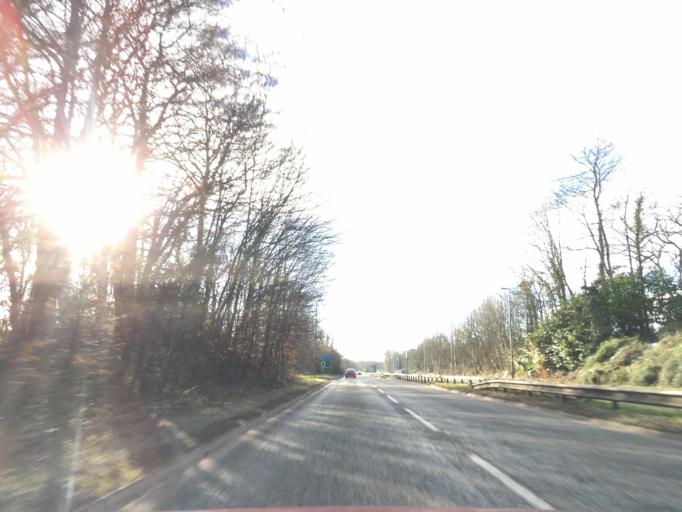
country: GB
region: Wales
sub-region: Torfaen County Borough
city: New Inn
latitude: 51.7134
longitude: -3.0005
